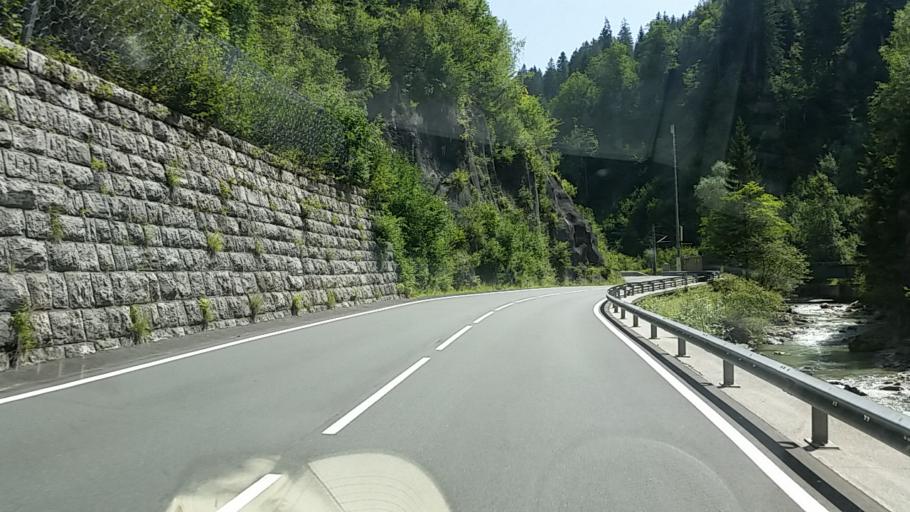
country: AT
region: Salzburg
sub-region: Politischer Bezirk Sankt Johann im Pongau
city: Bischofshofen
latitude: 47.4348
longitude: 13.2295
